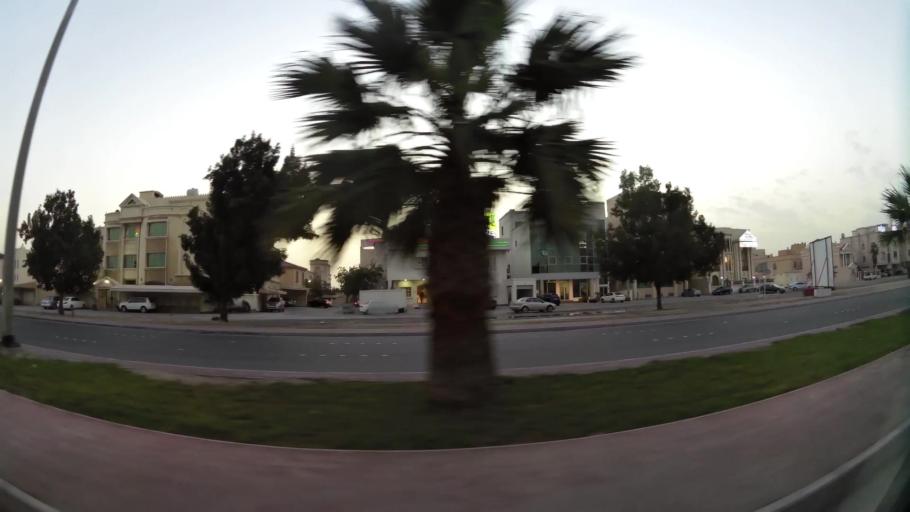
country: BH
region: Manama
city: Manama
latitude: 26.2083
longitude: 50.5671
